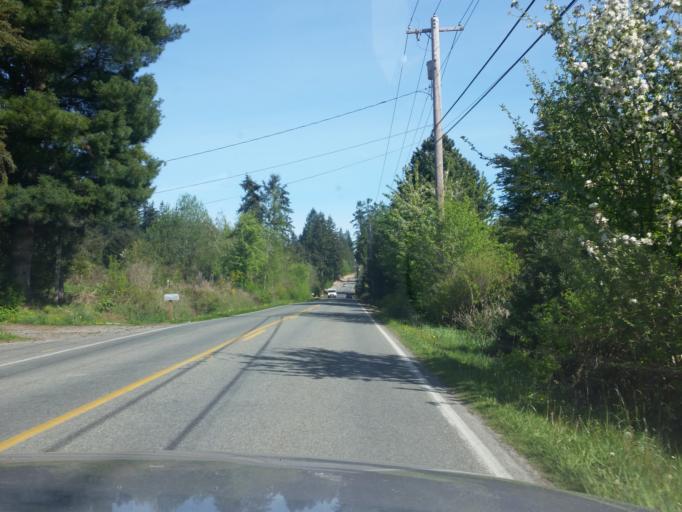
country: US
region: Washington
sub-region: Snohomish County
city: Maltby
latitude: 47.8164
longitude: -122.1100
